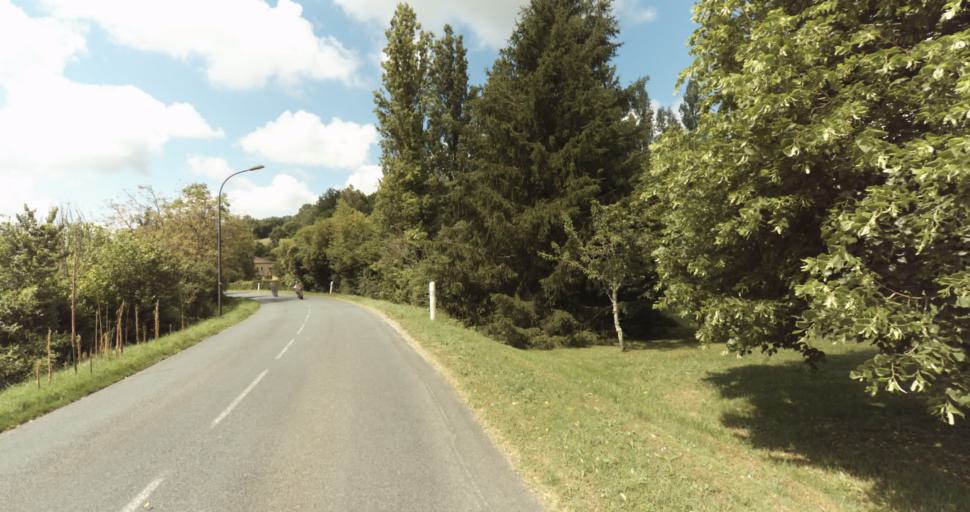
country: FR
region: Aquitaine
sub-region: Departement de la Dordogne
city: Beaumont-du-Perigord
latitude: 44.7768
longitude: 0.8149
